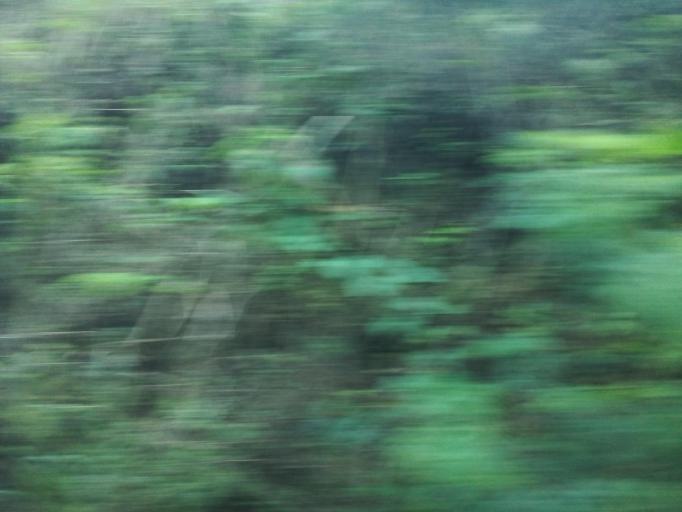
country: BR
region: Minas Gerais
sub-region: Joao Monlevade
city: Joao Monlevade
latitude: -19.8253
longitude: -43.1052
